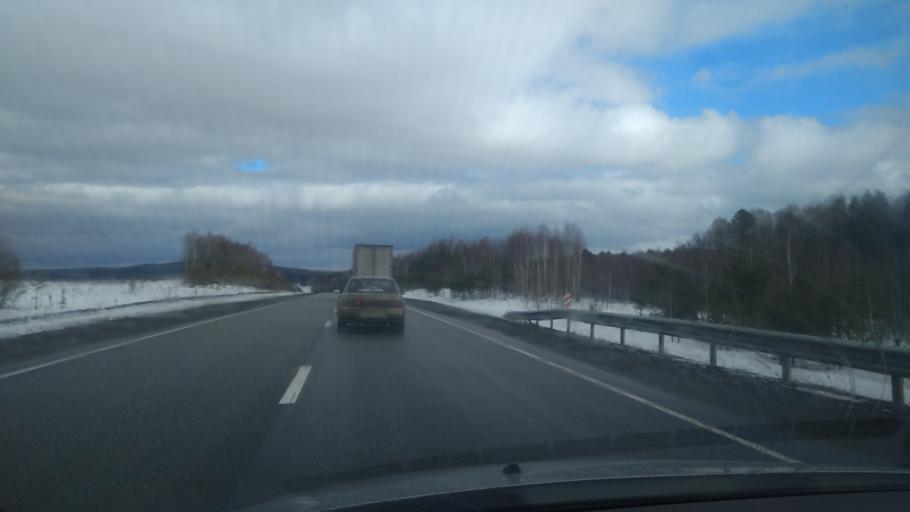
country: RU
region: Sverdlovsk
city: Bisert'
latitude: 56.8152
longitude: 58.7468
